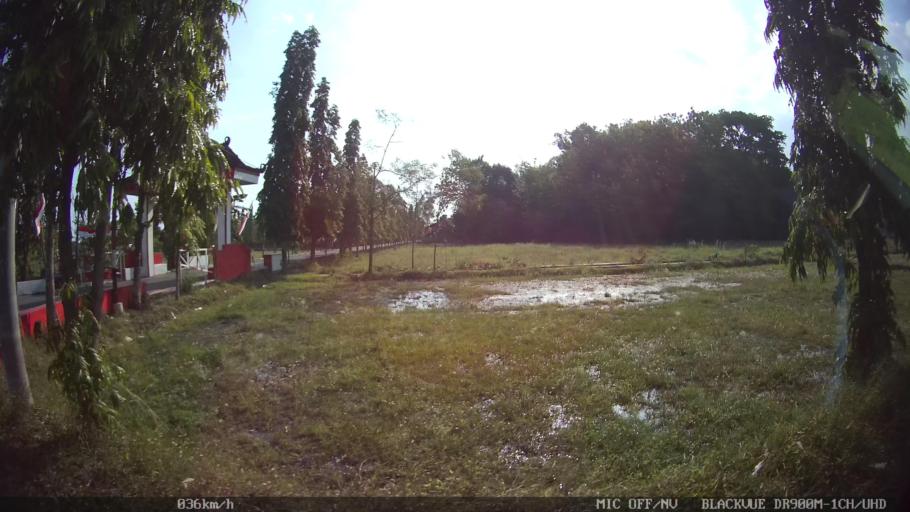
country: ID
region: Daerah Istimewa Yogyakarta
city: Kasihan
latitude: -7.8377
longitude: 110.3442
